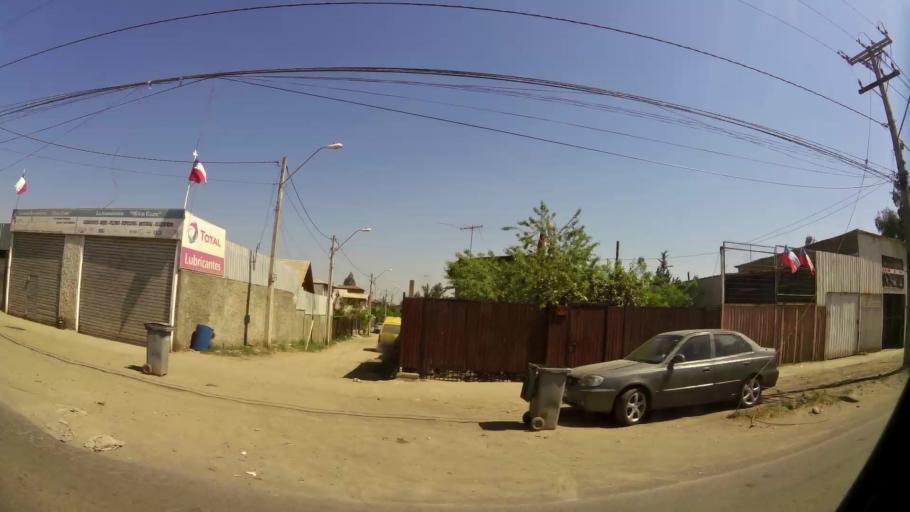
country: CL
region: Santiago Metropolitan
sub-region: Provincia de Talagante
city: Penaflor
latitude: -33.5801
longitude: -70.8113
